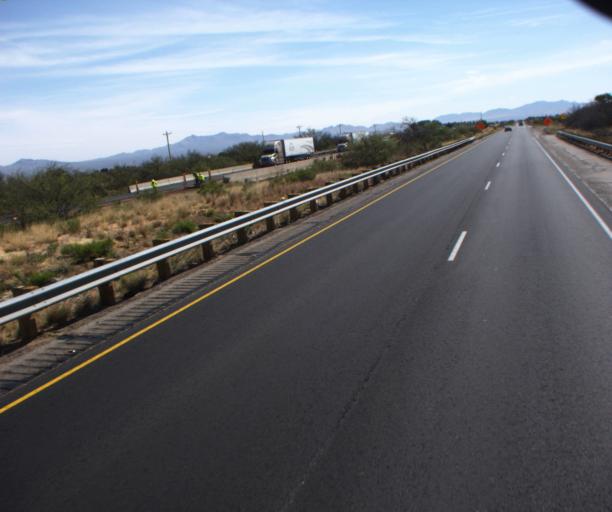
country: US
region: Arizona
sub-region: Cochise County
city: Mescal
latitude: 31.9629
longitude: -110.4019
